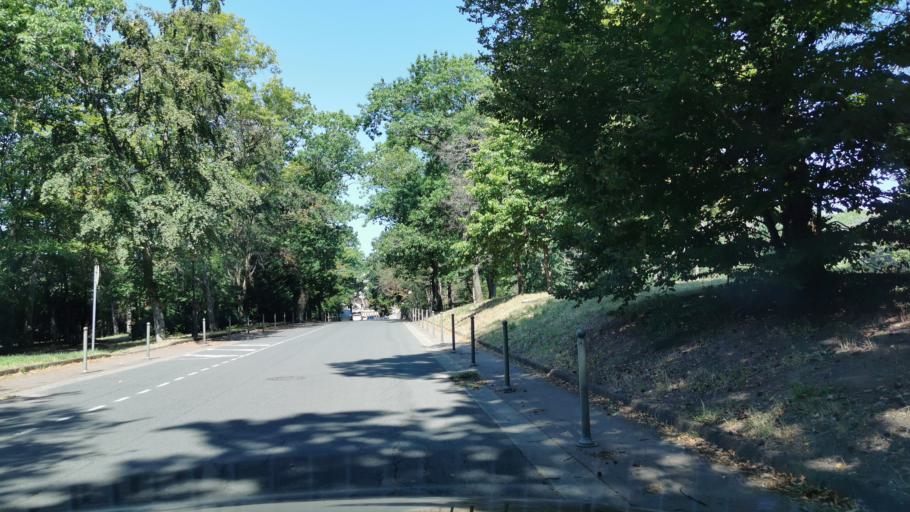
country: FR
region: Bourgogne
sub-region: Departement de Saone-et-Loire
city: Le Creusot
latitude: 46.8004
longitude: 4.4231
